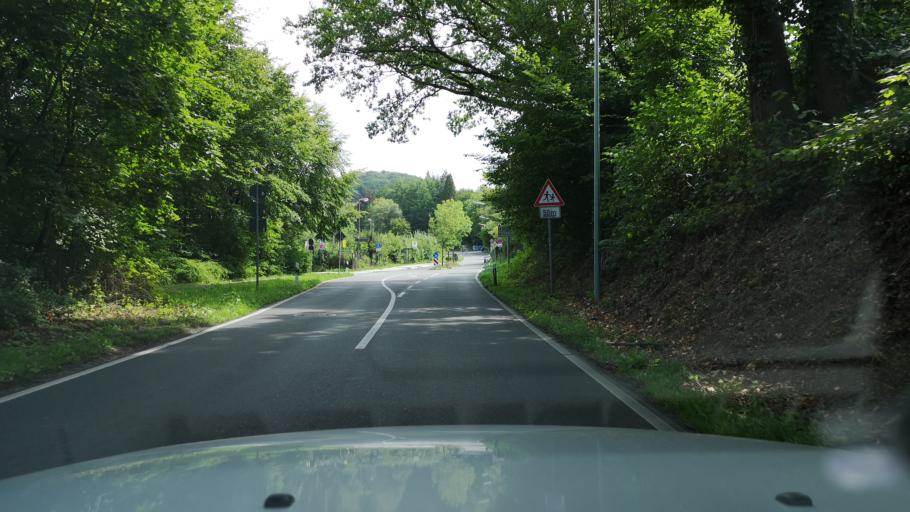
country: DE
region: North Rhine-Westphalia
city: Hattingen
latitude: 51.3446
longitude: 7.1303
